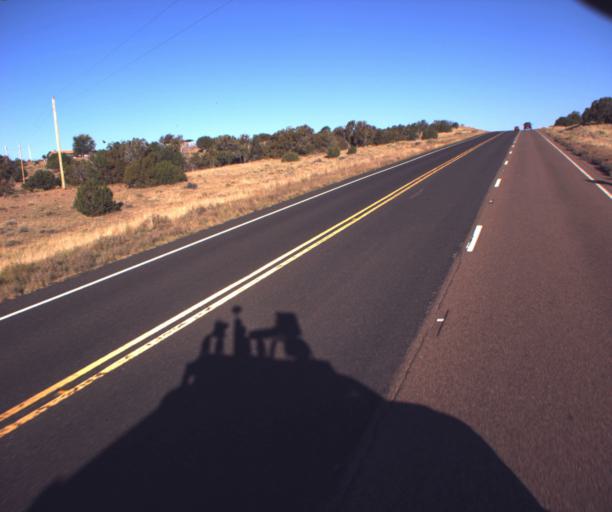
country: US
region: Arizona
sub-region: Apache County
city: Ganado
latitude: 35.4303
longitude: -109.5186
